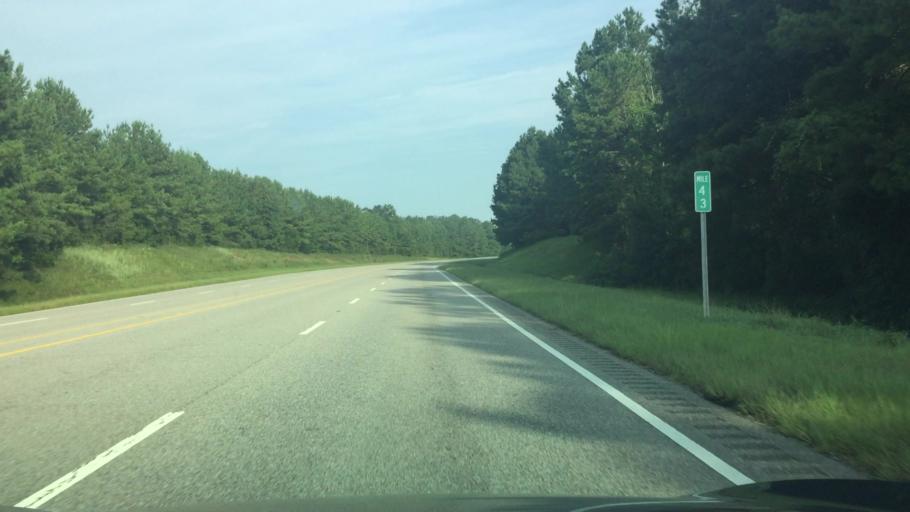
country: US
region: Alabama
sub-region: Butler County
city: Georgiana
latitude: 31.4668
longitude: -86.6602
